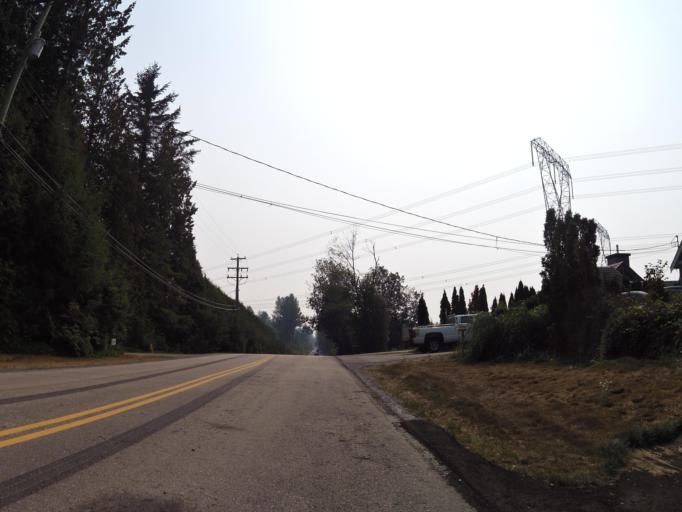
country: US
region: Washington
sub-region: Whatcom County
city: Blaine
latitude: 49.0287
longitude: -122.7573
